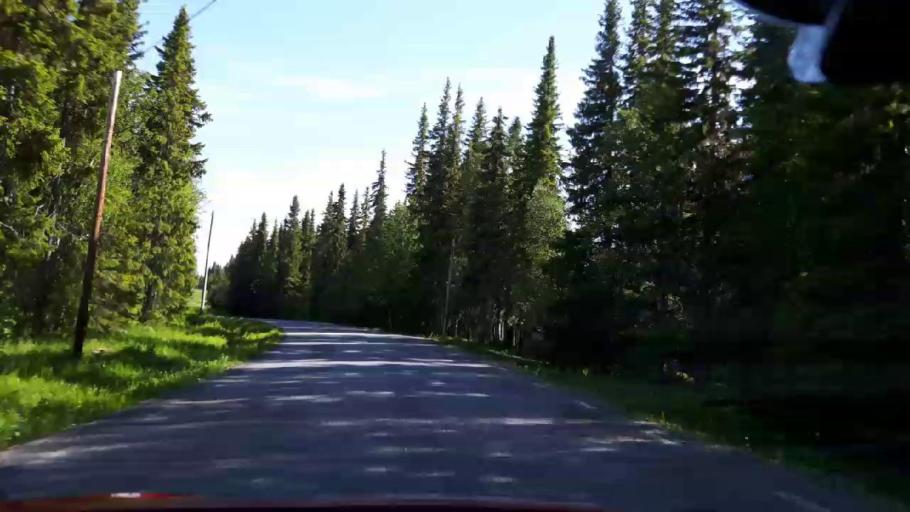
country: SE
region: Jaemtland
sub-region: Krokoms Kommun
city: Valla
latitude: 63.7336
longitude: 14.1176
